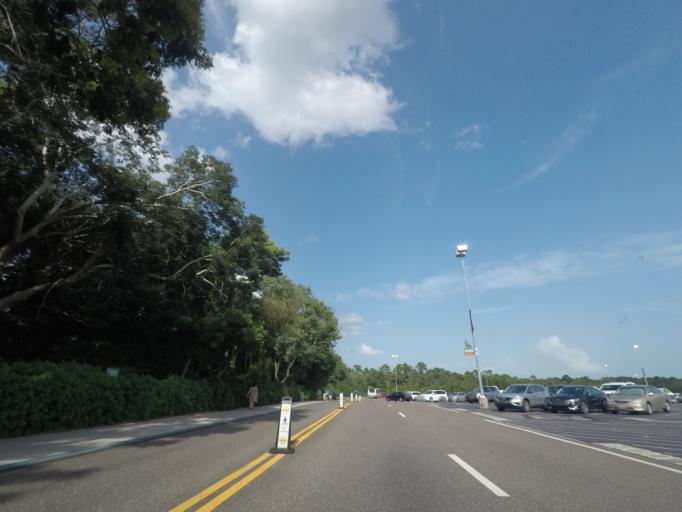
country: US
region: Florida
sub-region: Polk County
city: Citrus Ridge
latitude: 28.3530
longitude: -81.5869
